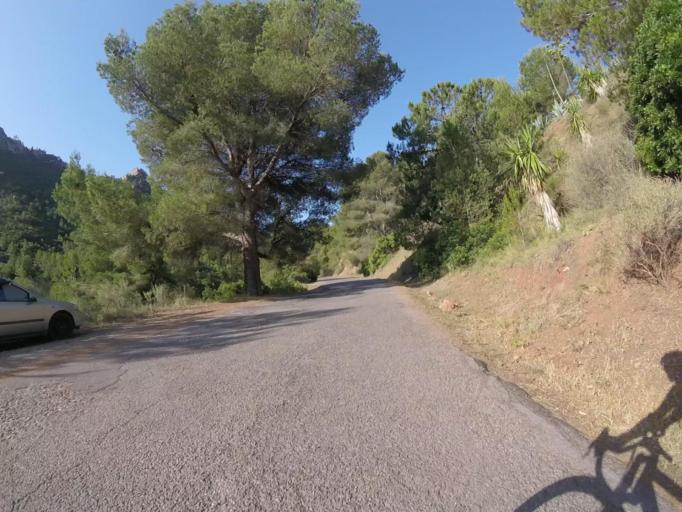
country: ES
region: Valencia
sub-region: Provincia de Castello
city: Benicassim
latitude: 40.0814
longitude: 0.0526
